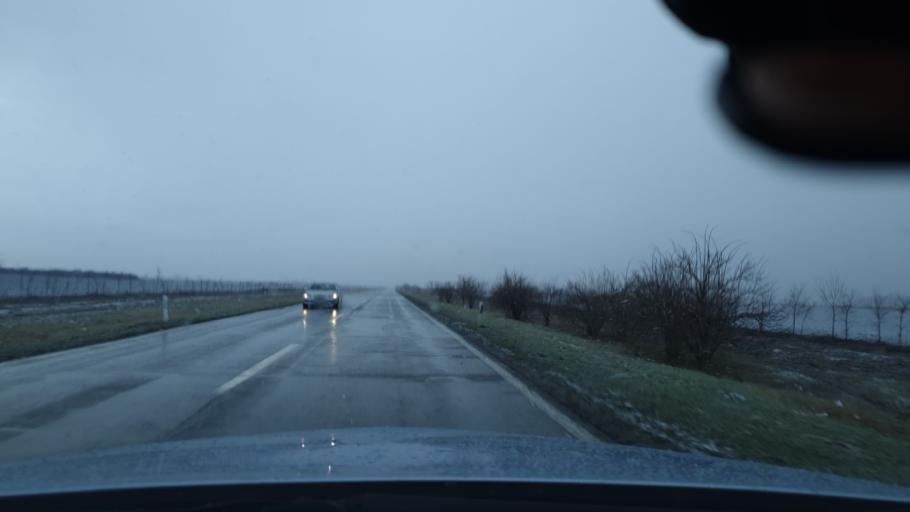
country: RS
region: Autonomna Pokrajina Vojvodina
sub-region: Juznobanatski Okrug
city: Pancevo
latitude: 44.8568
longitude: 20.7537
